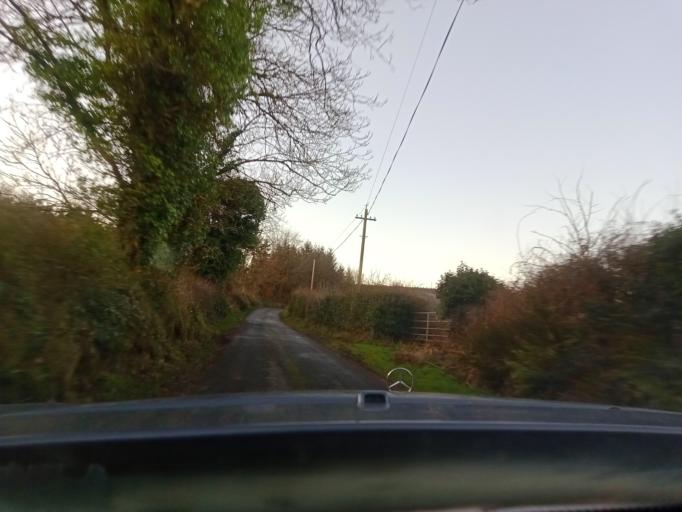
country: IE
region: Leinster
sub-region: Kilkenny
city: Graiguenamanagh
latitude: 52.4816
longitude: -6.9443
